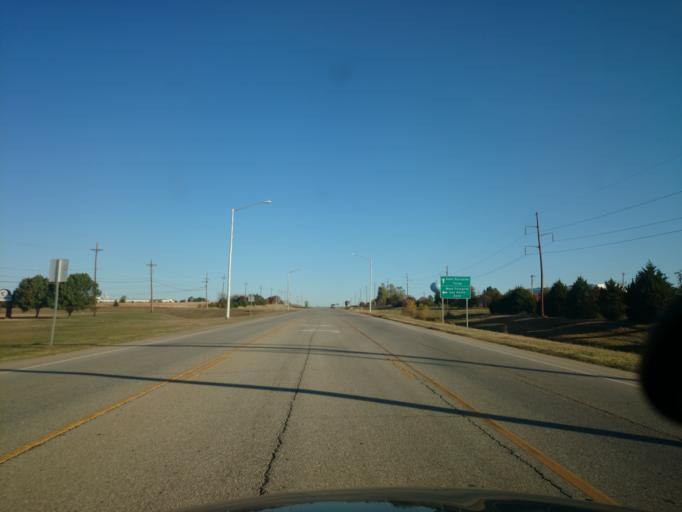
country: US
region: Oklahoma
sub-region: Payne County
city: Stillwater
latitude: 36.1723
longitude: -97.0518
